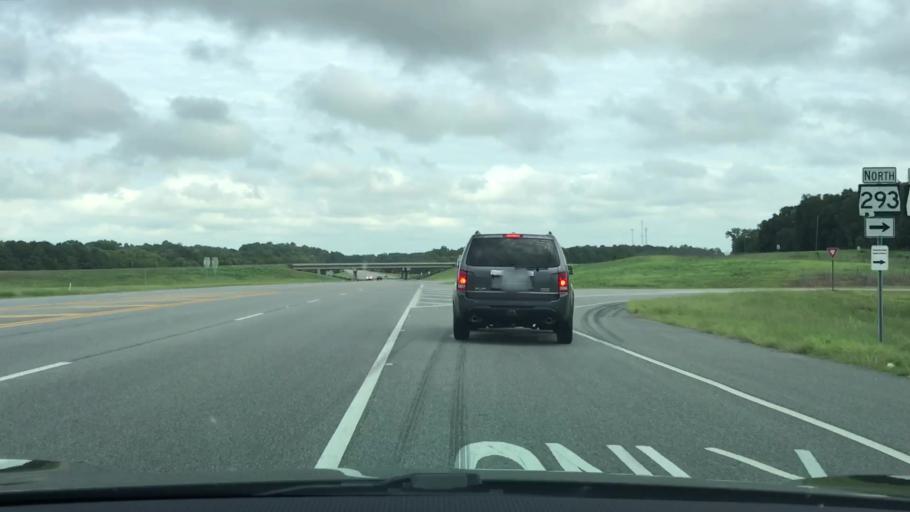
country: US
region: Alabama
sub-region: Montgomery County
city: Pike Road
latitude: 32.3354
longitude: -86.0599
